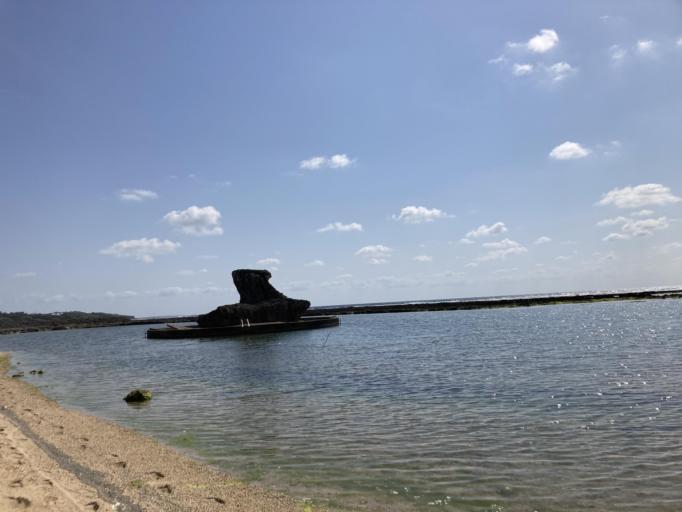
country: JP
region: Okinawa
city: Itoman
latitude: 26.1159
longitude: 127.7448
